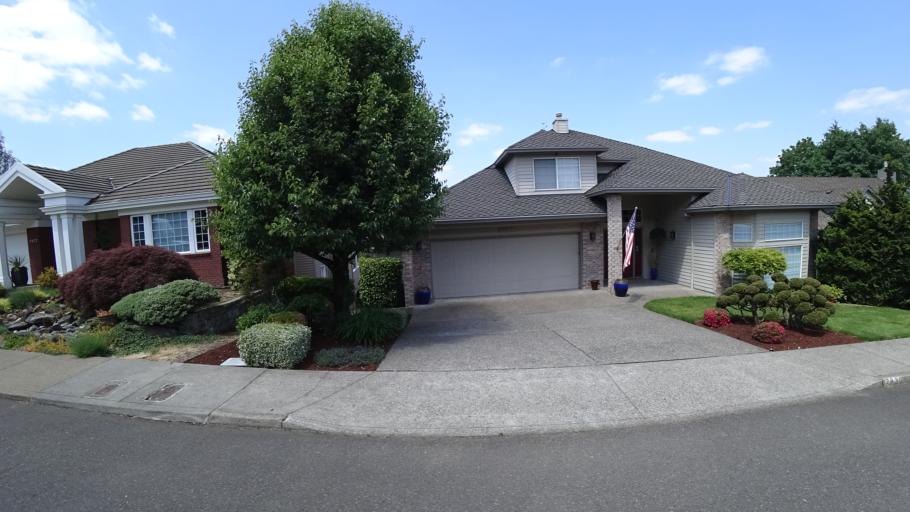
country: US
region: Oregon
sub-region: Clackamas County
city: Happy Valley
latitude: 45.4662
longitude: -122.5198
